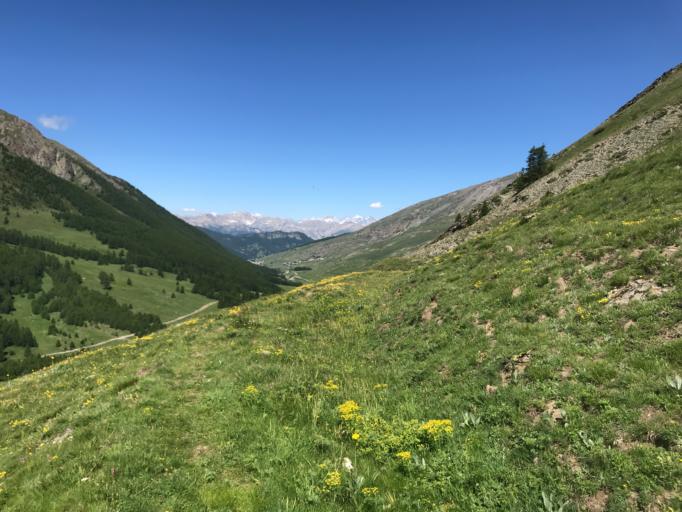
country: IT
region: Piedmont
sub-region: Provincia di Cuneo
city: Pontechianale
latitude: 44.7117
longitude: 6.9272
